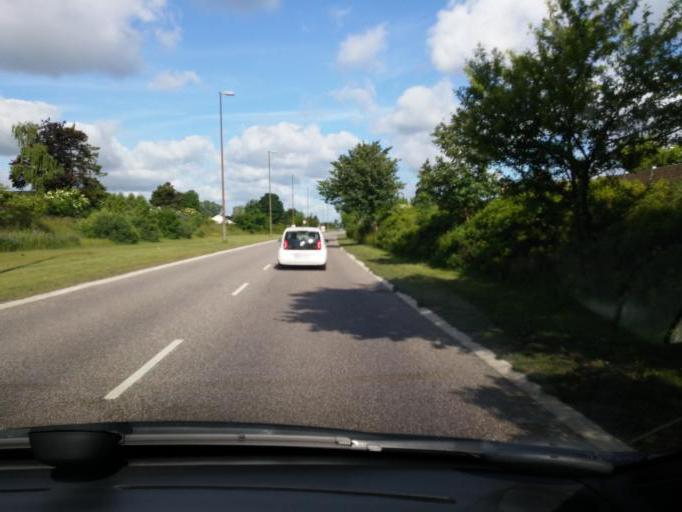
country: DK
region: Zealand
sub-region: Greve Kommune
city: Greve
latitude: 55.5991
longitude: 12.3133
